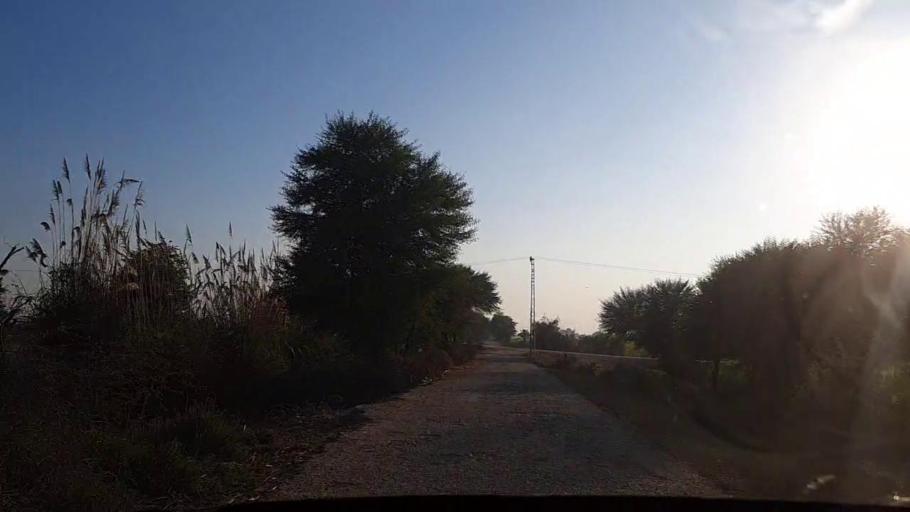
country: PK
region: Sindh
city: Sobhadero
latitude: 27.4008
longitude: 68.3894
